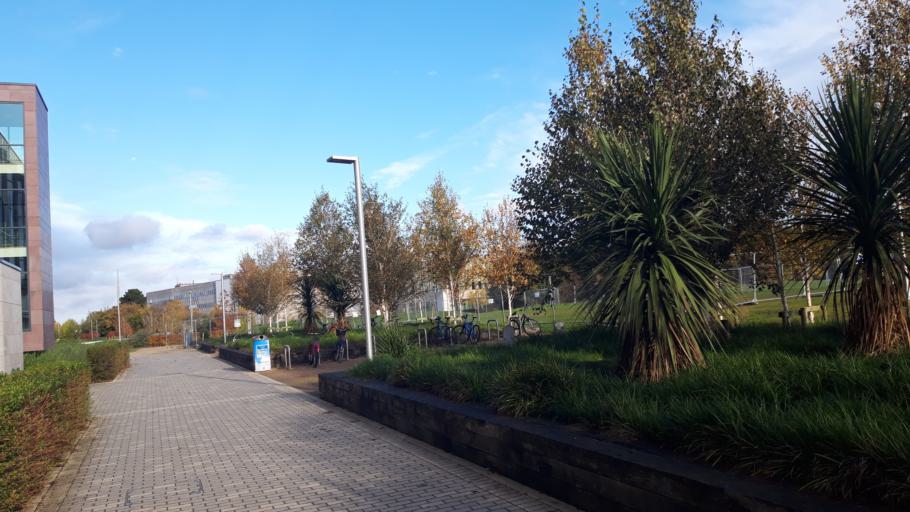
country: IE
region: Leinster
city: Mount Merrion
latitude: 53.3043
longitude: -6.2183
